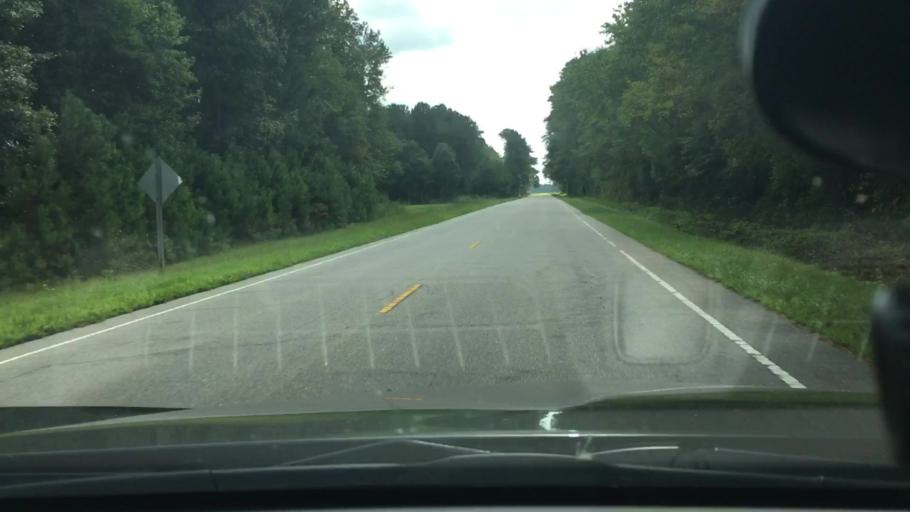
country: US
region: North Carolina
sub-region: Edgecombe County
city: Pinetops
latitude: 35.7597
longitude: -77.5556
